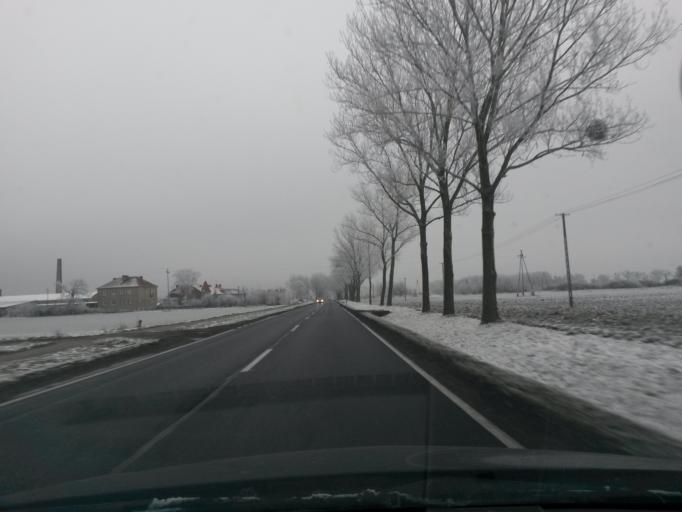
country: PL
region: Kujawsko-Pomorskie
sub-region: Powiat inowroclawski
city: Gniewkowo
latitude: 52.9017
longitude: 18.4443
